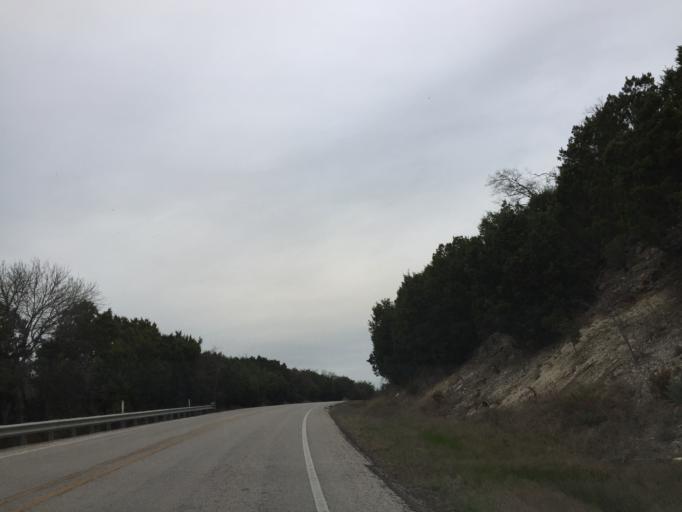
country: US
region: Texas
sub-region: Coryell County
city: Ames
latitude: 31.5053
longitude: -97.7273
